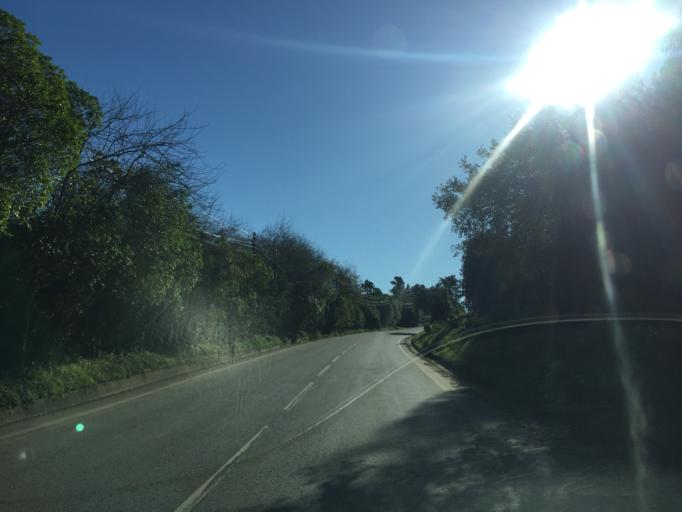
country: PT
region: Lisbon
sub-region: Sintra
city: Almargem
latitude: 38.8082
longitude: -9.2891
